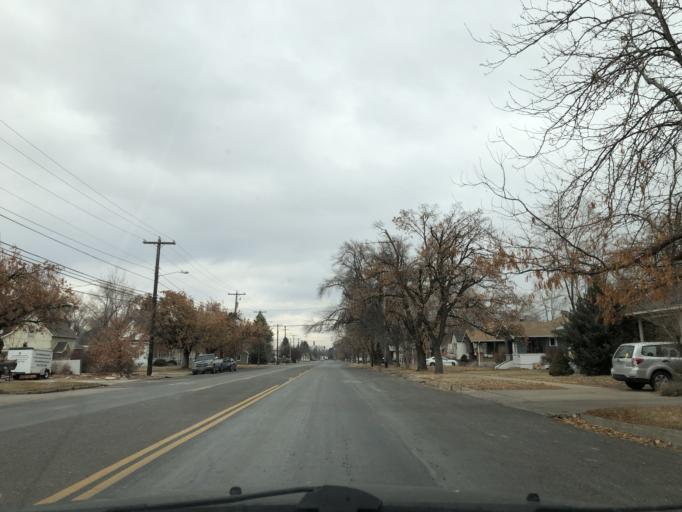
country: US
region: Utah
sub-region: Cache County
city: Logan
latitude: 41.7374
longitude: -111.8374
